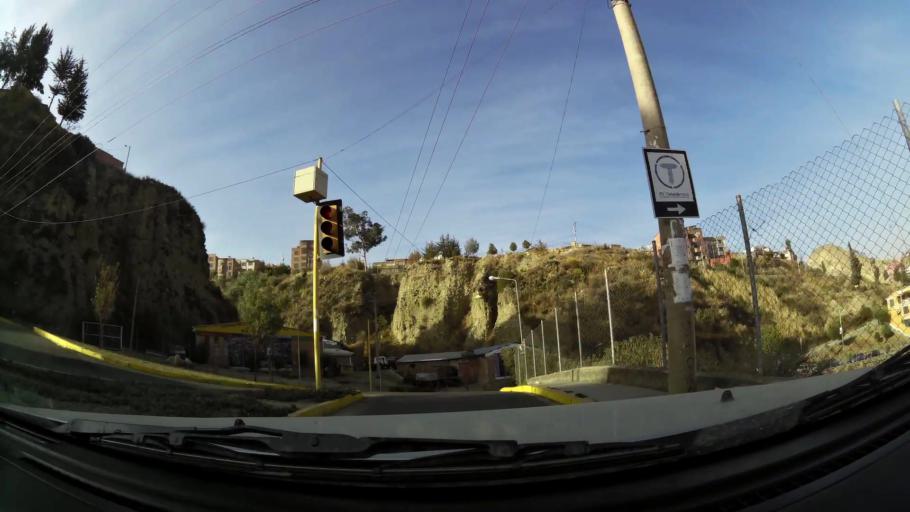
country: BO
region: La Paz
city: La Paz
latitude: -16.5249
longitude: -68.1032
